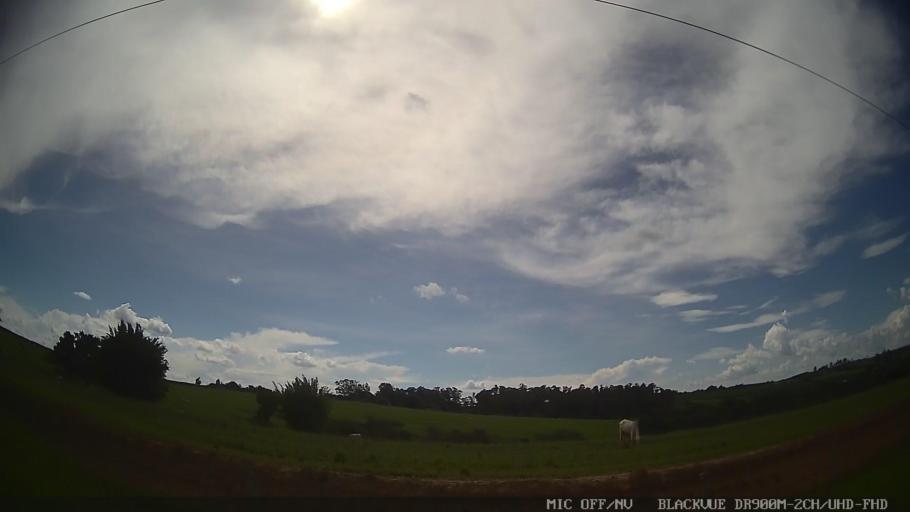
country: BR
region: Sao Paulo
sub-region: Conchas
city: Conchas
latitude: -22.9673
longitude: -47.9839
